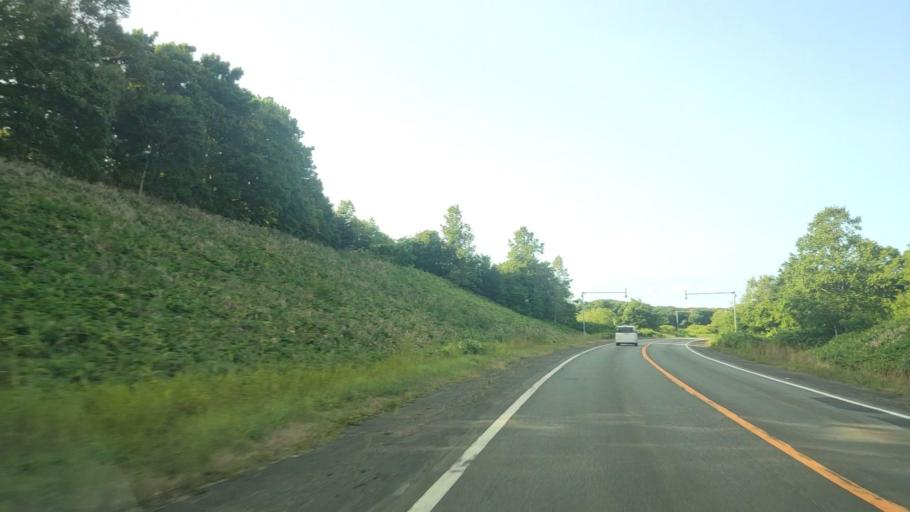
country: JP
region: Hokkaido
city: Makubetsu
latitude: 45.0672
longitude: 141.7481
